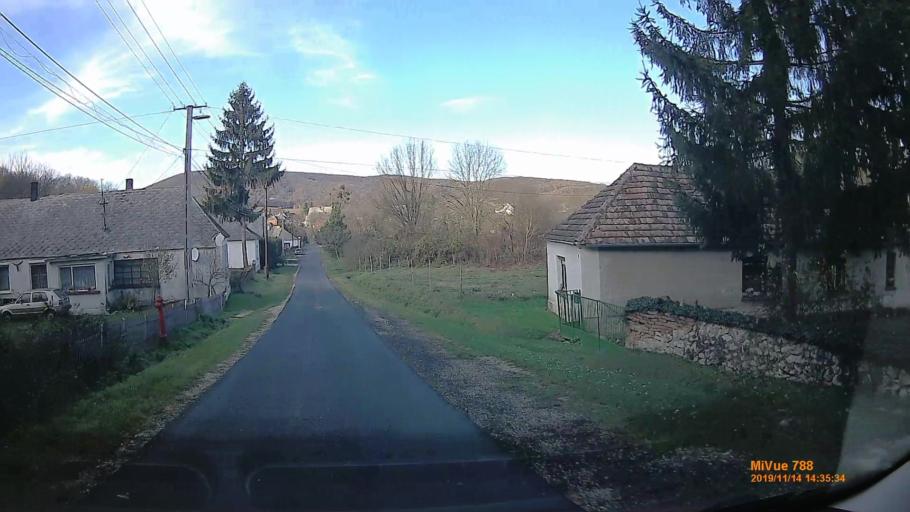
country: HU
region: Veszprem
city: Zirc
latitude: 47.2261
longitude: 17.7906
